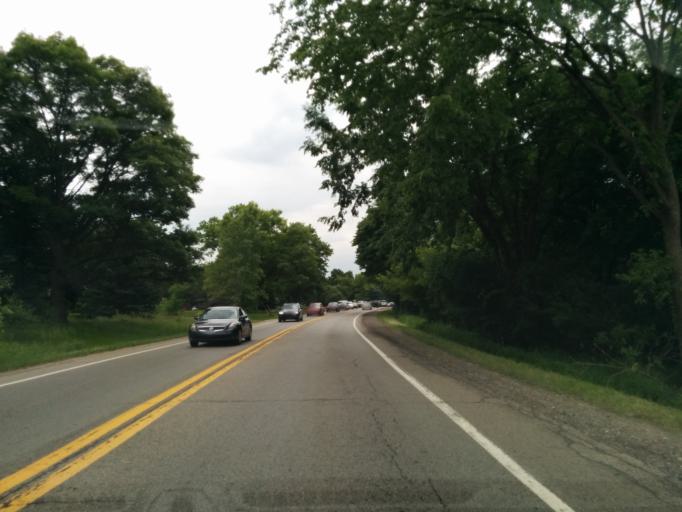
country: US
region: Michigan
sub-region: Oakland County
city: Wolverine Lake
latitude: 42.5396
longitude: -83.4372
